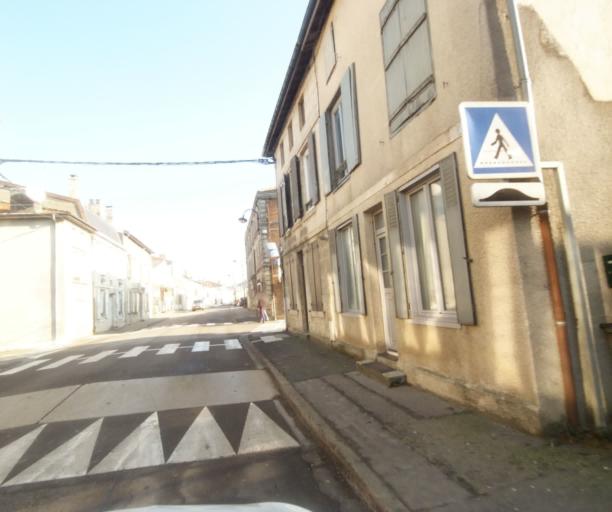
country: FR
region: Champagne-Ardenne
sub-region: Departement de la Haute-Marne
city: Wassy
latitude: 48.4981
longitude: 4.9444
